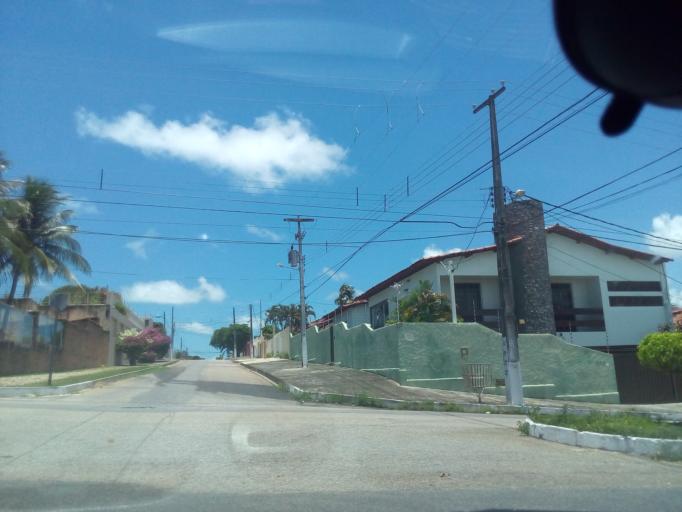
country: BR
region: Rio Grande do Norte
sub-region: Natal
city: Natal
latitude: -5.8465
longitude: -35.2068
